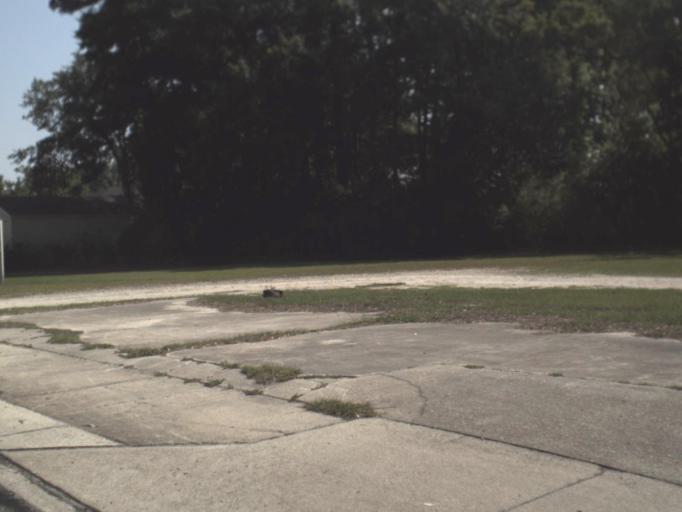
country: US
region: Florida
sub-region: Duval County
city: Jacksonville
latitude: 30.2977
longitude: -81.7518
